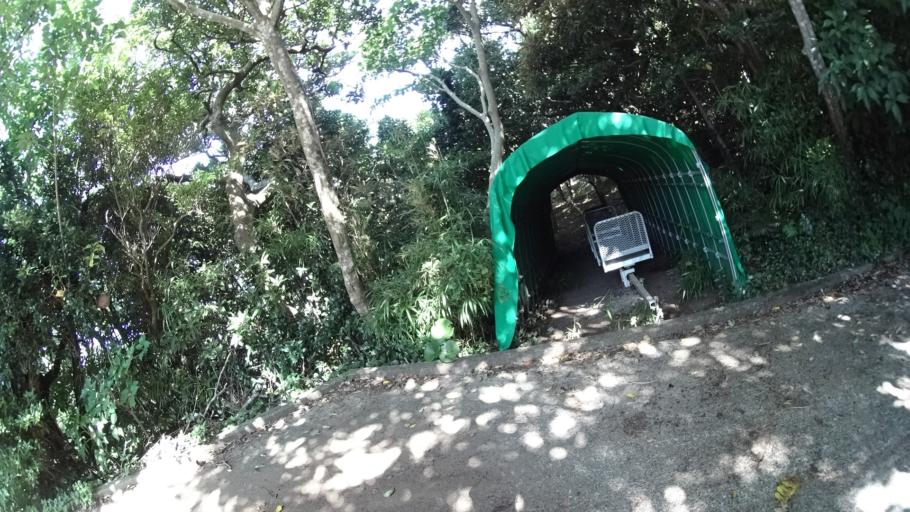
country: JP
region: Shizuoka
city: Shimoda
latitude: 34.5141
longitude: 139.2749
